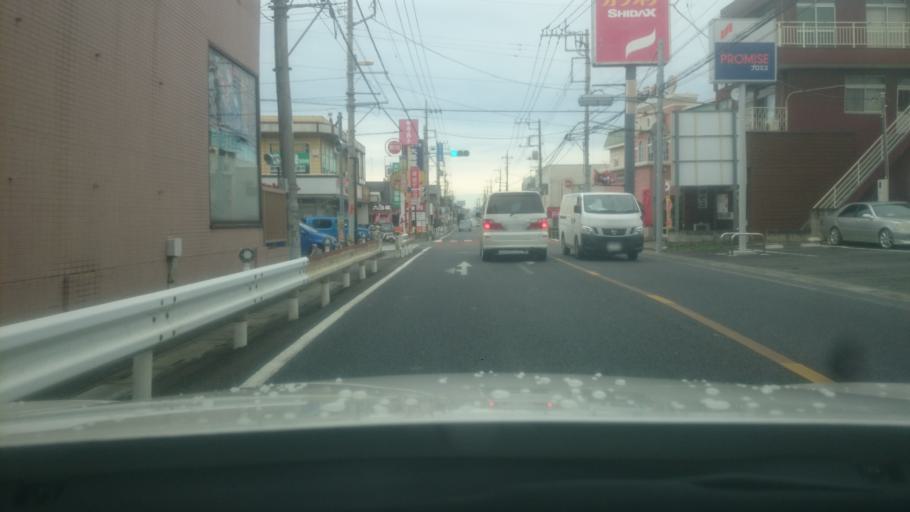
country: JP
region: Saitama
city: Kamifukuoka
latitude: 35.8822
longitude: 139.4964
